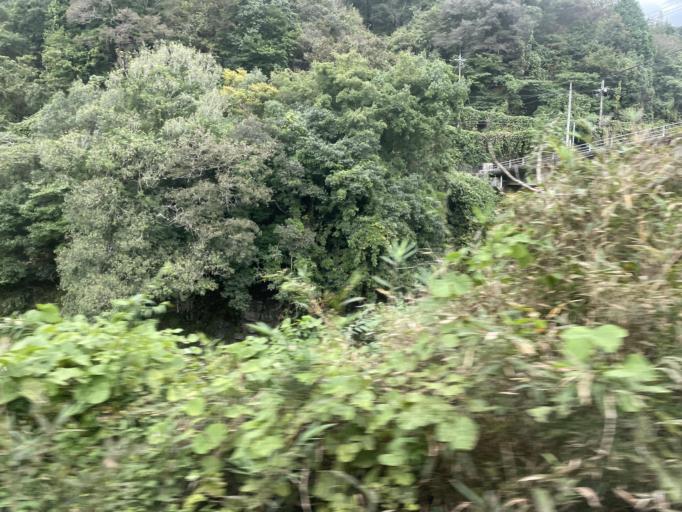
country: JP
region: Hyogo
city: Sasayama
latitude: 35.0774
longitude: 135.1396
